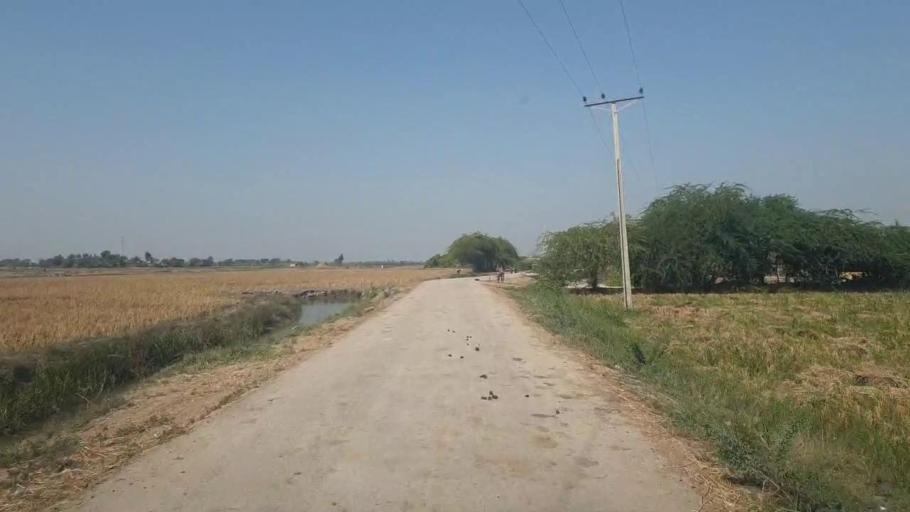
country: PK
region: Sindh
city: Badin
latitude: 24.6799
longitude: 68.9010
